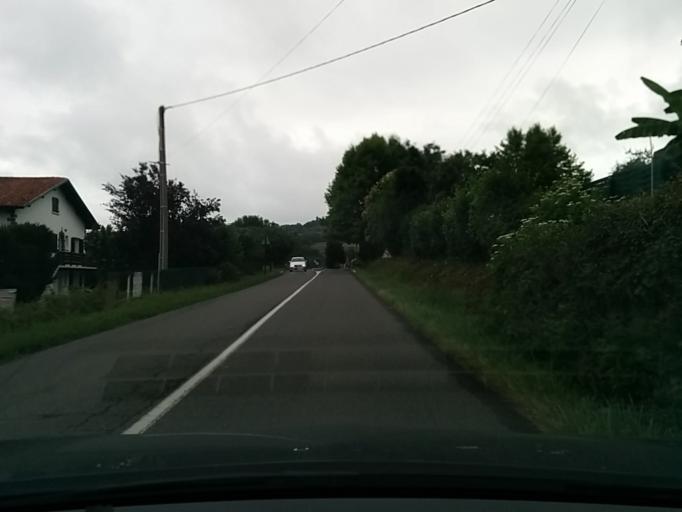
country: FR
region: Aquitaine
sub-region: Departement des Pyrenees-Atlantiques
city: Saint-Pee-sur-Nivelle
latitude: 43.3405
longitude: -1.5497
